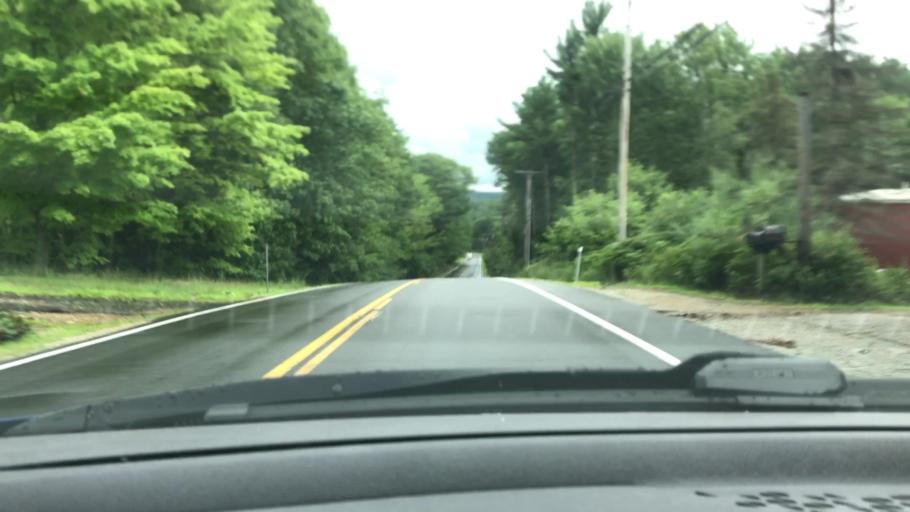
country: US
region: New Hampshire
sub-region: Rockingham County
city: Candia
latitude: 43.1624
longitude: -71.2433
